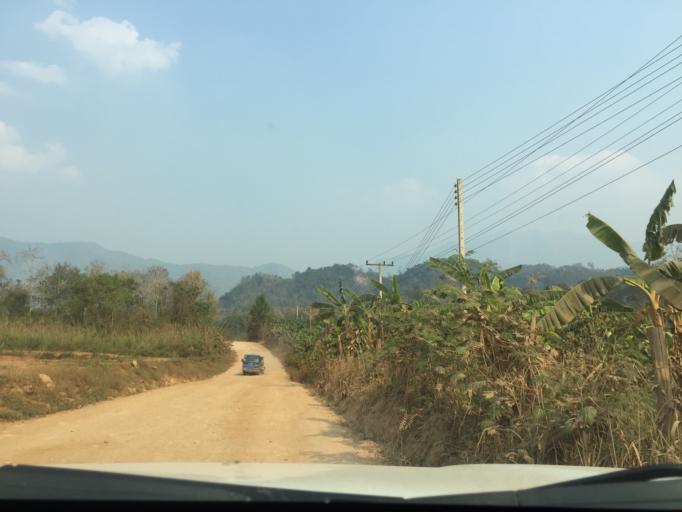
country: LA
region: Xiagnabouli
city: Sainyabuli
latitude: 19.2108
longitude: 101.6947
